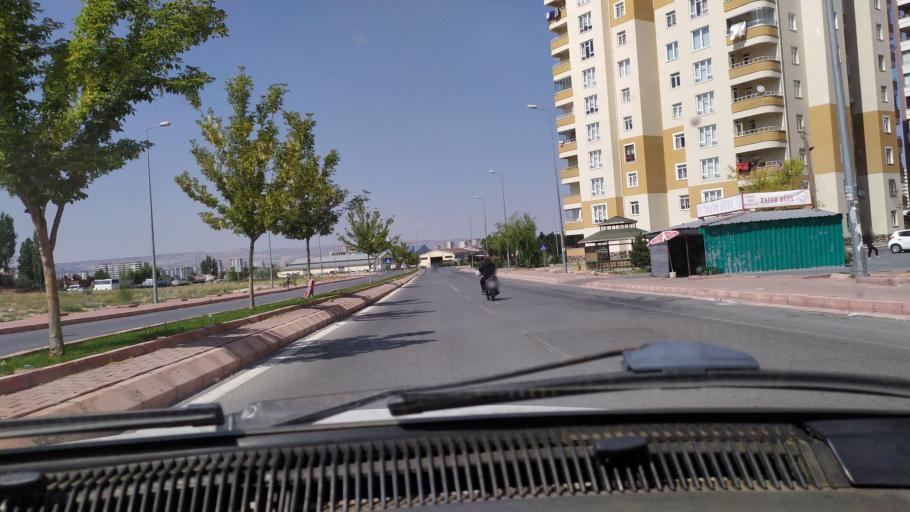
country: TR
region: Kayseri
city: Talas
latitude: 38.7176
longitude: 35.5556
